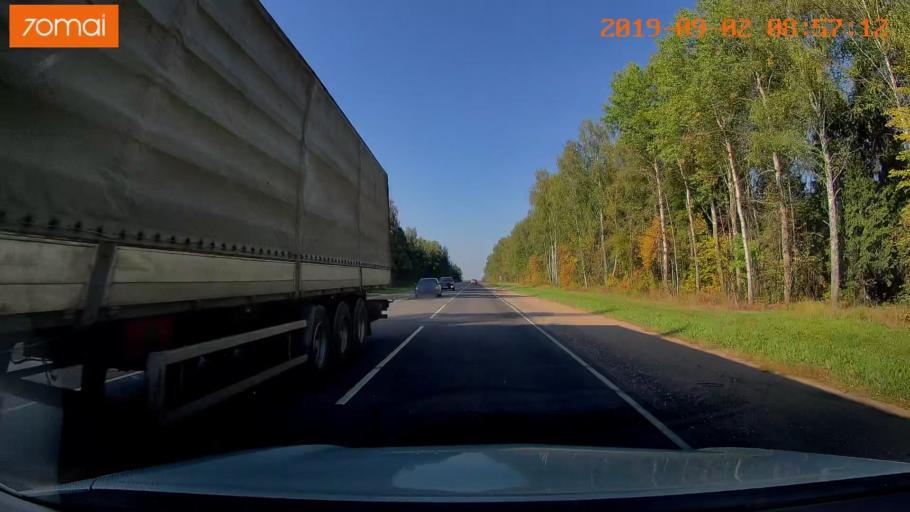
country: RU
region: Kaluga
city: Medyn'
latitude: 54.9388
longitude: 35.7739
